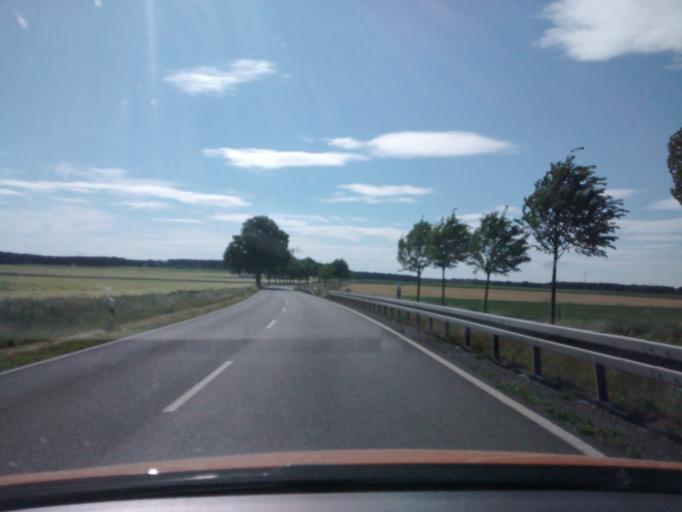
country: DE
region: Brandenburg
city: Juterbog
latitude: 51.9852
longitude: 13.1631
